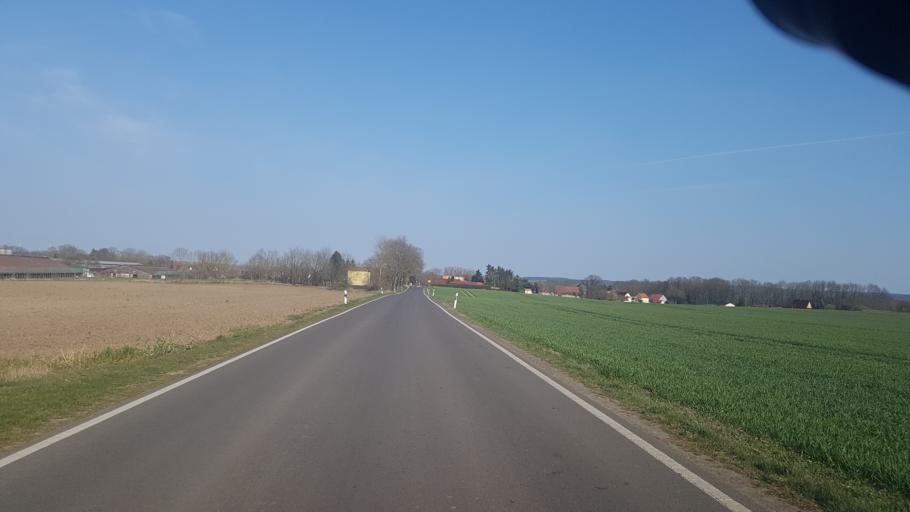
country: DE
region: Brandenburg
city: Gerswalde
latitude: 53.2179
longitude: 13.8312
